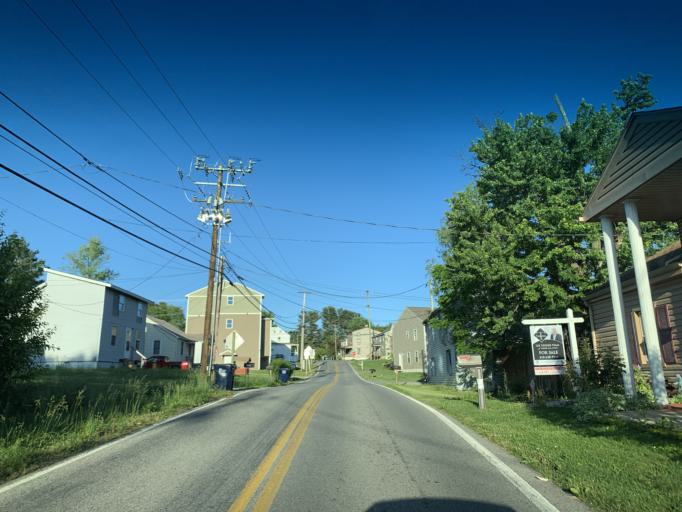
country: US
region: Maryland
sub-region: Cecil County
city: Elkton
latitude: 39.6635
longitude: -75.8546
